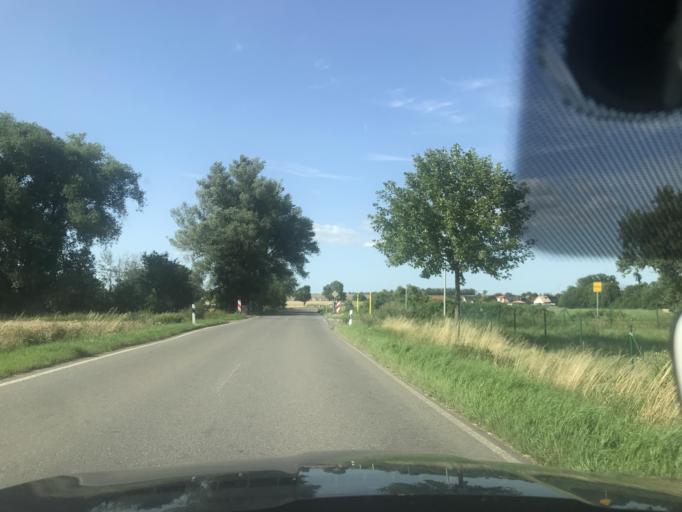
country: DE
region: Saxony-Anhalt
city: Wegeleben
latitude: 51.8839
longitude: 11.1613
